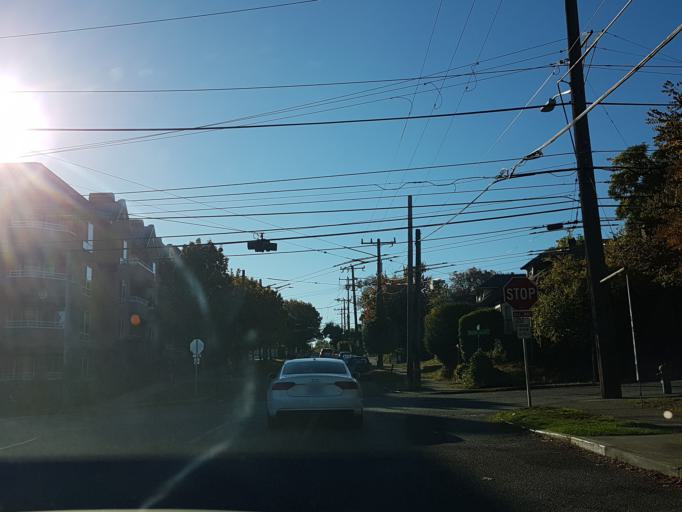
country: US
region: Washington
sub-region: King County
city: Seattle
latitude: 47.6263
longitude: -122.3459
